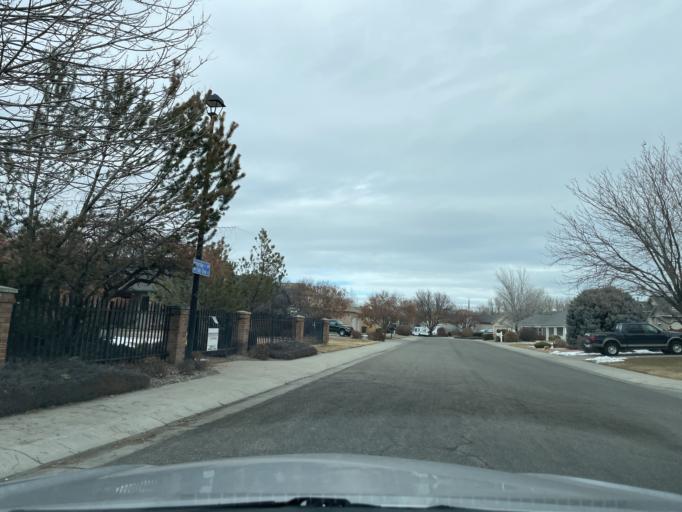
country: US
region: Colorado
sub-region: Mesa County
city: Grand Junction
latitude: 39.1038
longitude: -108.5822
